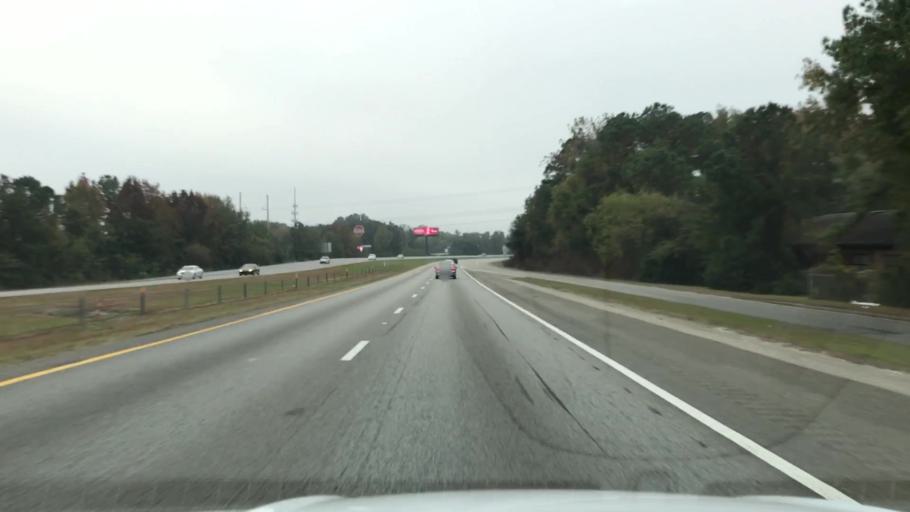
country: US
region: South Carolina
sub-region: Charleston County
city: North Charleston
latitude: 32.8511
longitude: -80.0196
